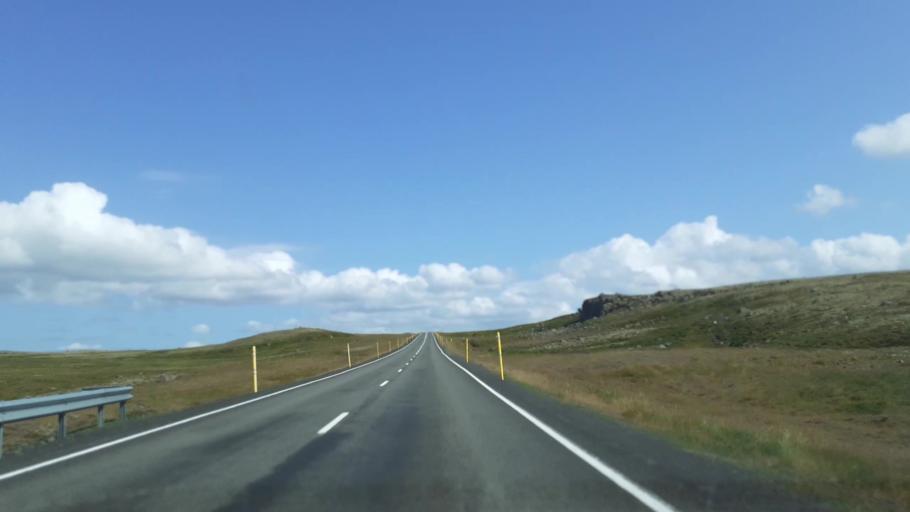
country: IS
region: West
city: Borgarnes
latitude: 64.9342
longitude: -21.0717
